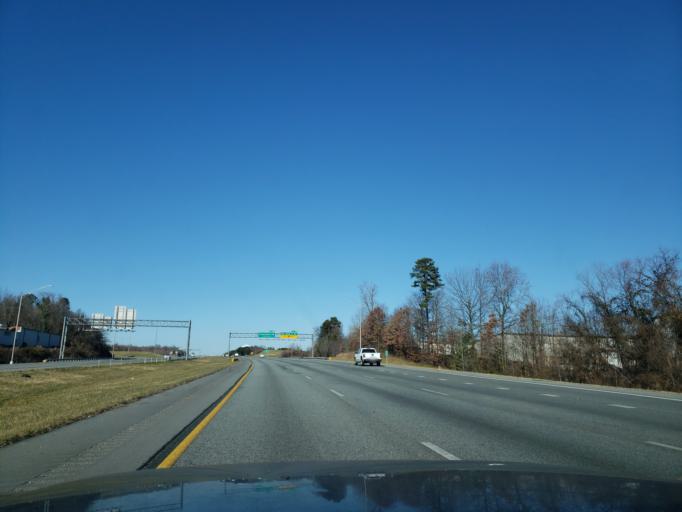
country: US
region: North Carolina
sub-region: Guilford County
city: High Point
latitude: 35.9601
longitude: -79.9747
